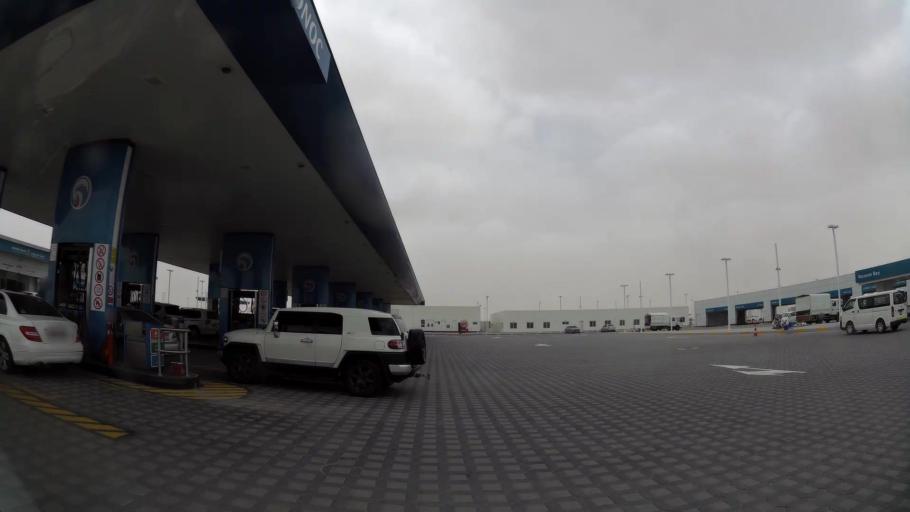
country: AE
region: Abu Dhabi
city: Abu Dhabi
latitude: 24.3982
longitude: 54.6906
